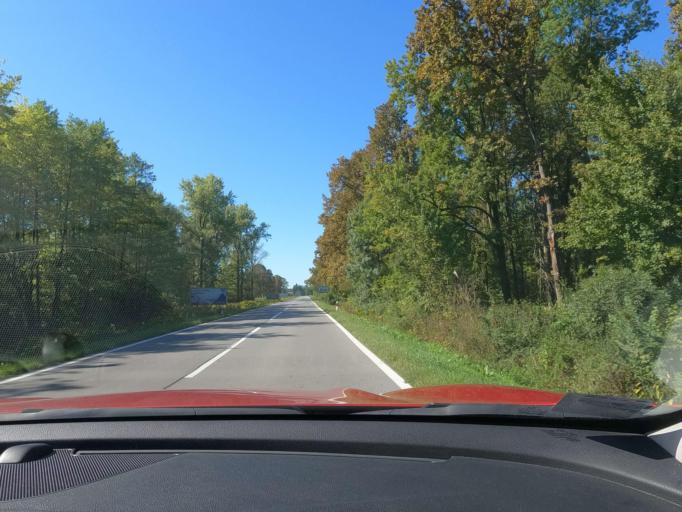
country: HR
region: Sisacko-Moslavacka
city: Budasevo
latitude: 45.4899
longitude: 16.4866
